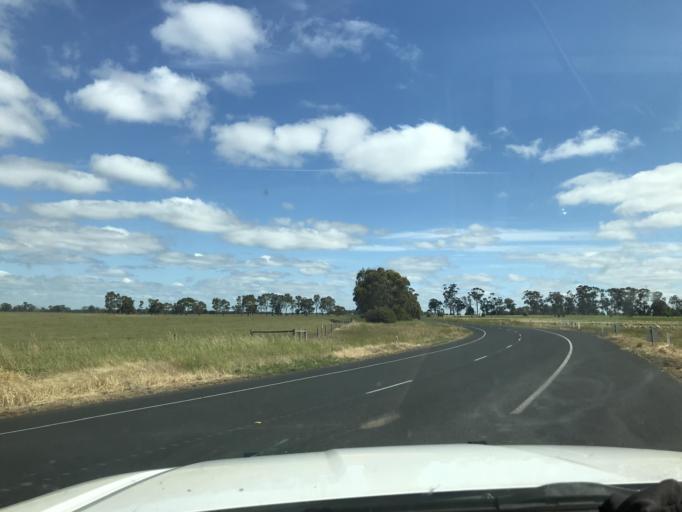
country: AU
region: South Australia
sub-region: Naracoorte and Lucindale
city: Naracoorte
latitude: -37.0213
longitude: 141.3067
